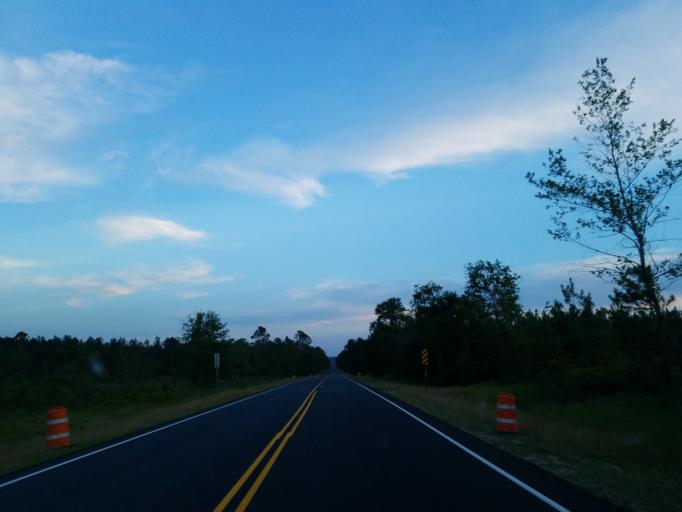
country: US
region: Georgia
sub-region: Turner County
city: Ashburn
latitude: 31.7002
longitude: -83.8081
